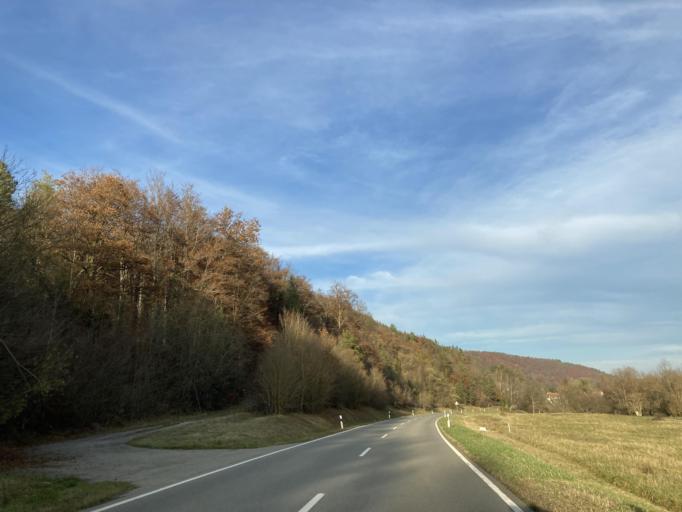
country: DE
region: Baden-Wuerttemberg
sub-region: Tuebingen Region
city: Hirrlingen
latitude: 48.4458
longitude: 8.8455
